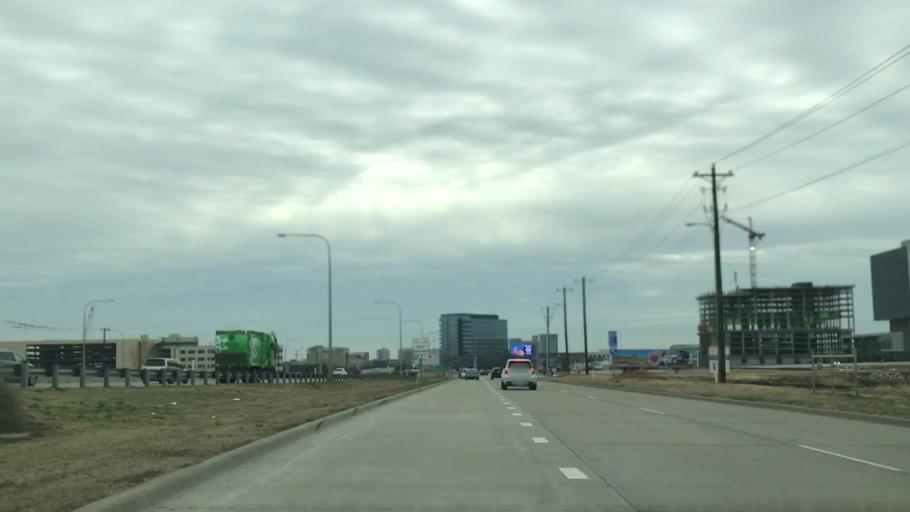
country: US
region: Texas
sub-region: Collin County
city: Frisco
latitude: 33.1132
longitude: -96.8239
